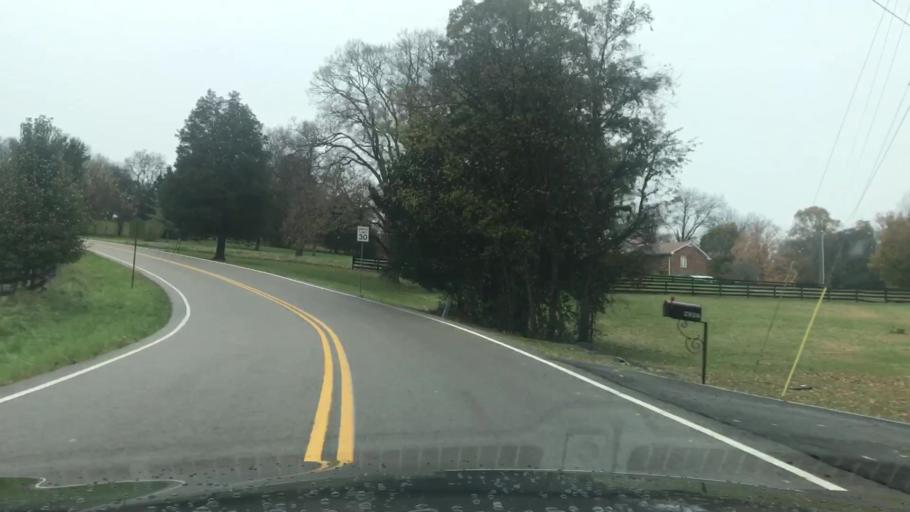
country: US
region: Tennessee
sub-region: Williamson County
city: Franklin
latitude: 35.8943
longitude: -86.8168
